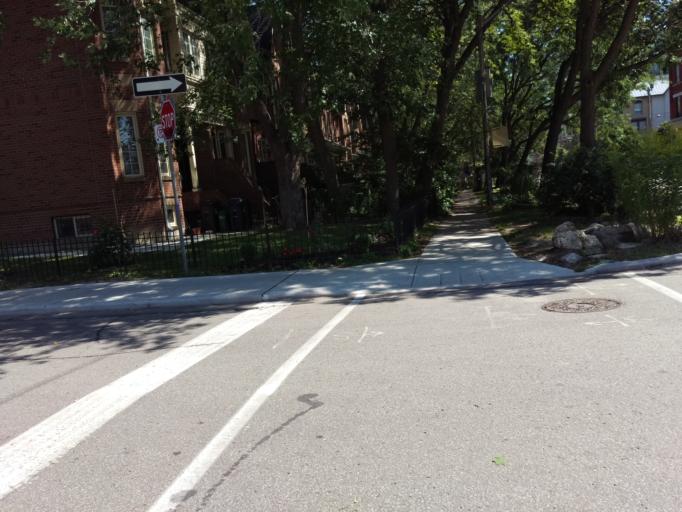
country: CA
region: Ontario
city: Toronto
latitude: 43.6505
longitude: -79.3950
